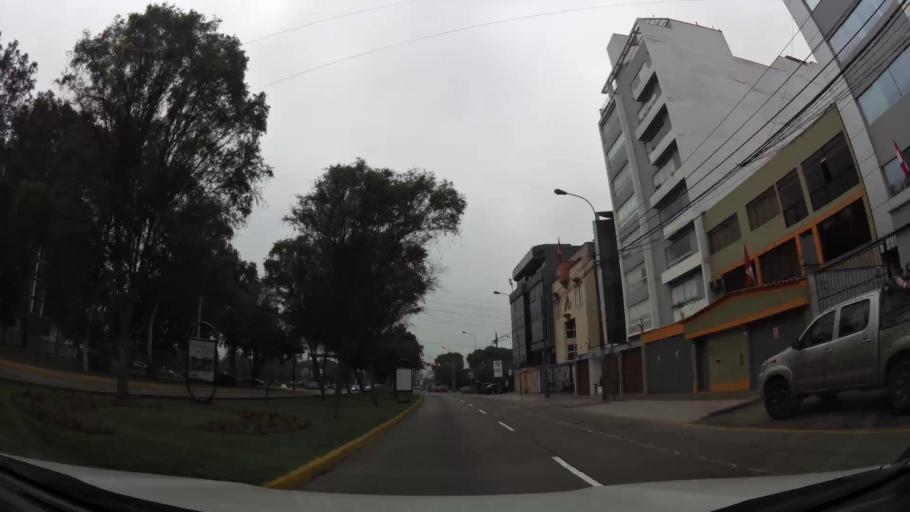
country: PE
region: Lima
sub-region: Lima
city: San Luis
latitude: -12.1025
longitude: -76.9909
